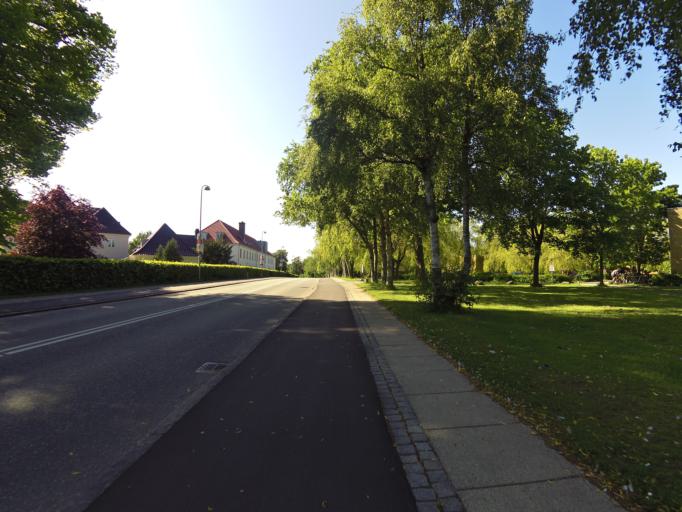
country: DK
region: Capital Region
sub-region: Gladsaxe Municipality
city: Buddinge
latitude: 55.7723
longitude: 12.4737
